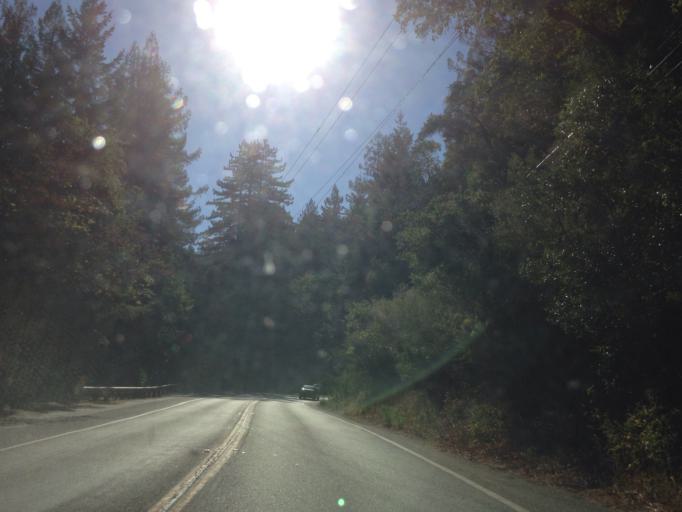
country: US
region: California
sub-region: Sonoma County
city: Monte Rio
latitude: 38.4746
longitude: -123.0036
